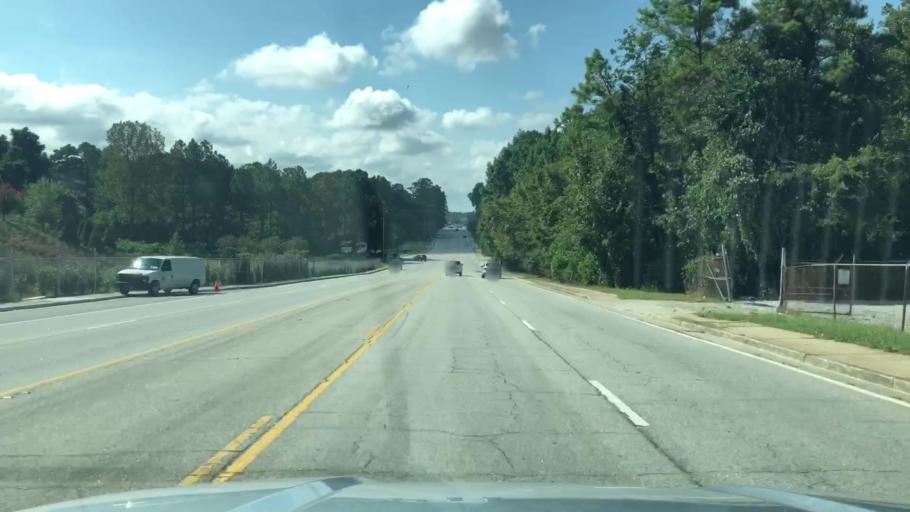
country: US
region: Georgia
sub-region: DeKalb County
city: Chamblee
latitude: 33.8742
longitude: -84.3095
